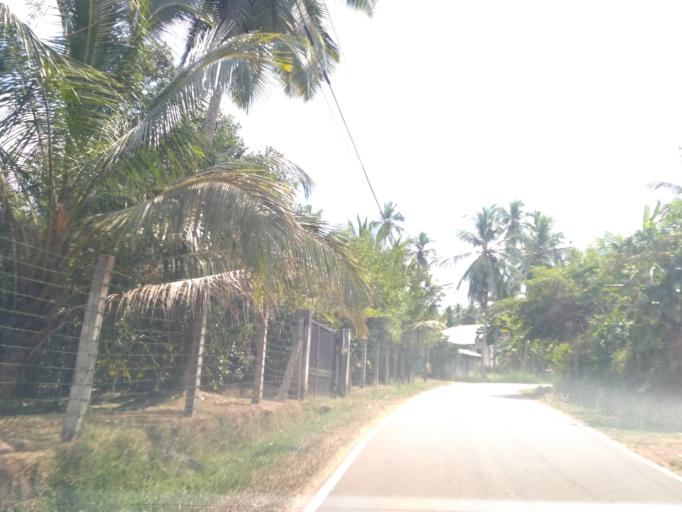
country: LK
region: North Western
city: Kuliyapitiya
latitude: 7.3310
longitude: 80.0632
